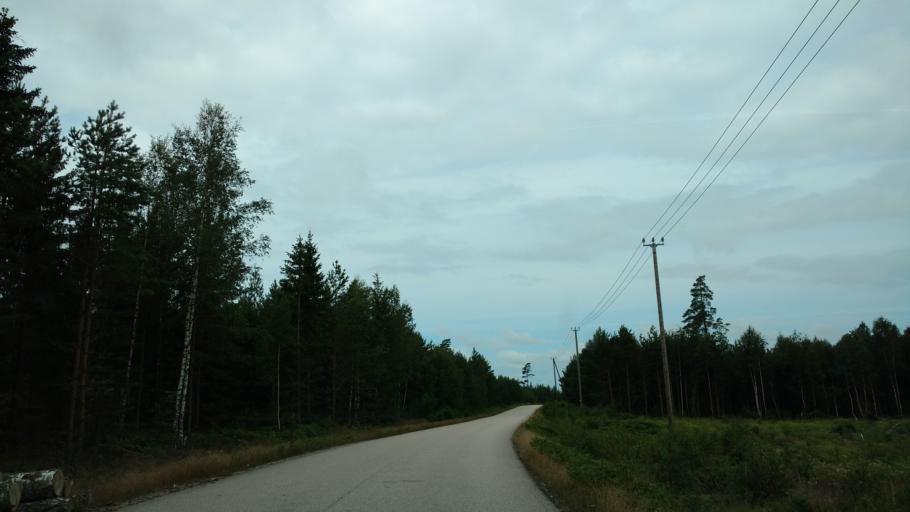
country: FI
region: Varsinais-Suomi
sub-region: Aboland-Turunmaa
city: Dragsfjaerd
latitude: 59.9462
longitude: 22.4037
